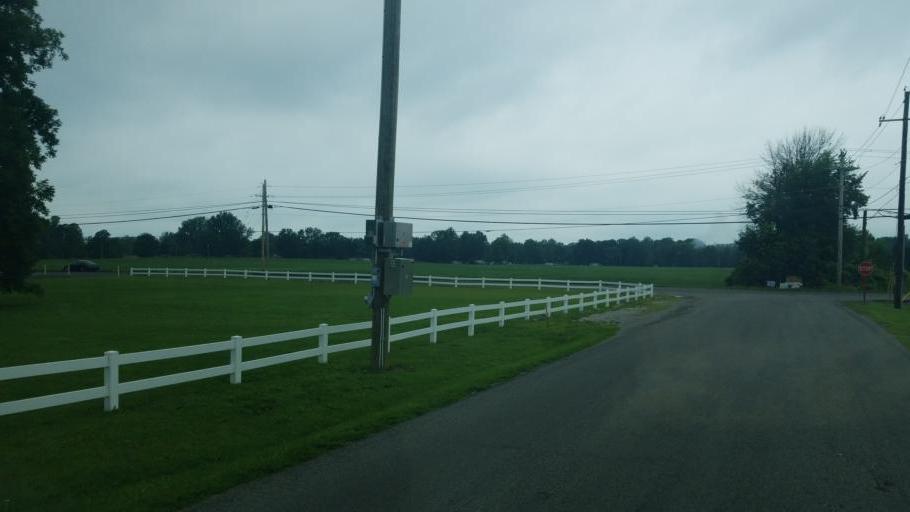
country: US
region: Ohio
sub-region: Logan County
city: Russells Point
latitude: 40.4693
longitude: -83.8585
